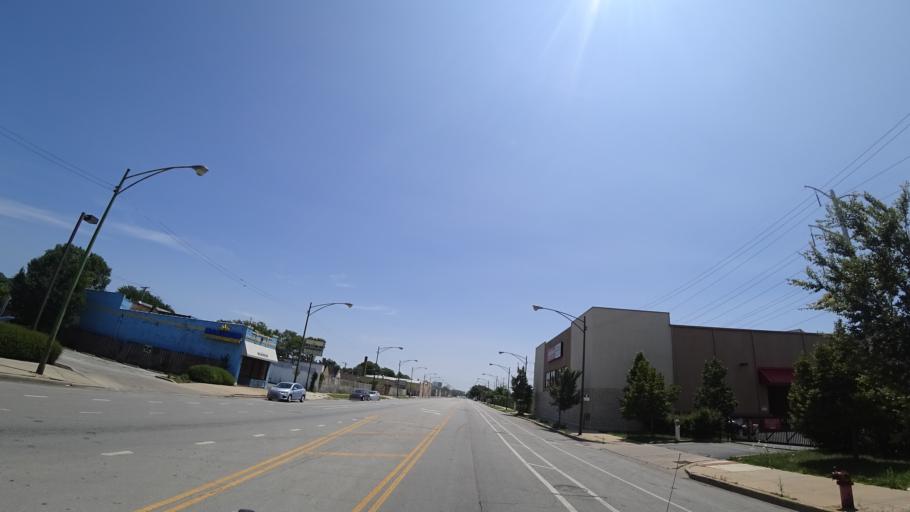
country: US
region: Indiana
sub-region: Lake County
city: Whiting
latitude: 41.7439
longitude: -87.5751
